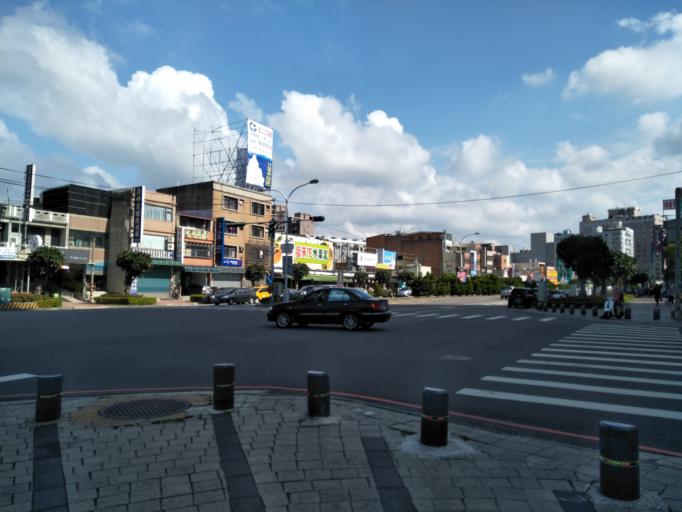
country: TW
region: Taiwan
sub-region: Hsinchu
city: Hsinchu
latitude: 24.6897
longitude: 120.9043
